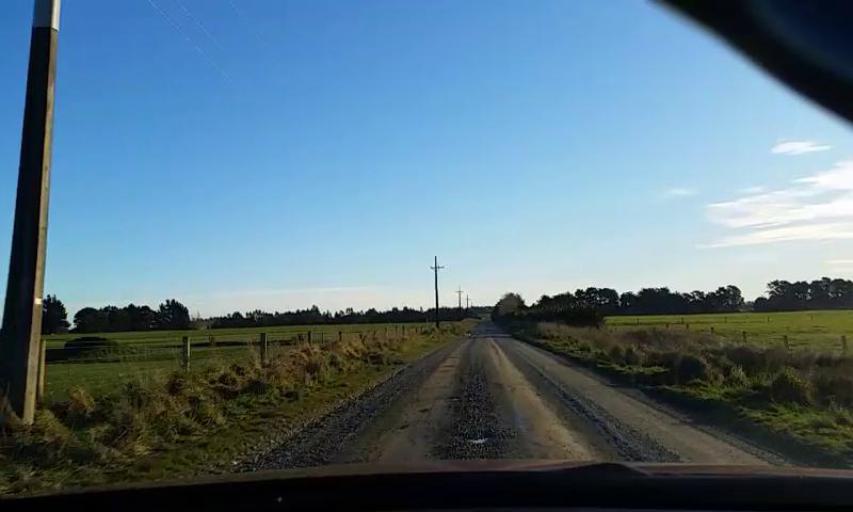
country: NZ
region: Southland
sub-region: Invercargill City
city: Invercargill
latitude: -46.2916
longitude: 168.4266
